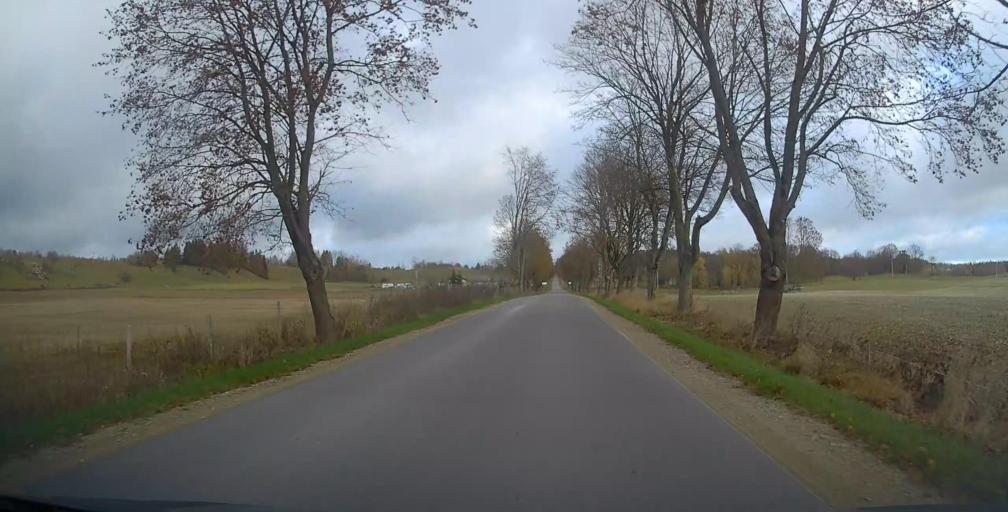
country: PL
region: Podlasie
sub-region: Suwalki
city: Suwalki
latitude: 54.3014
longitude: 22.8790
